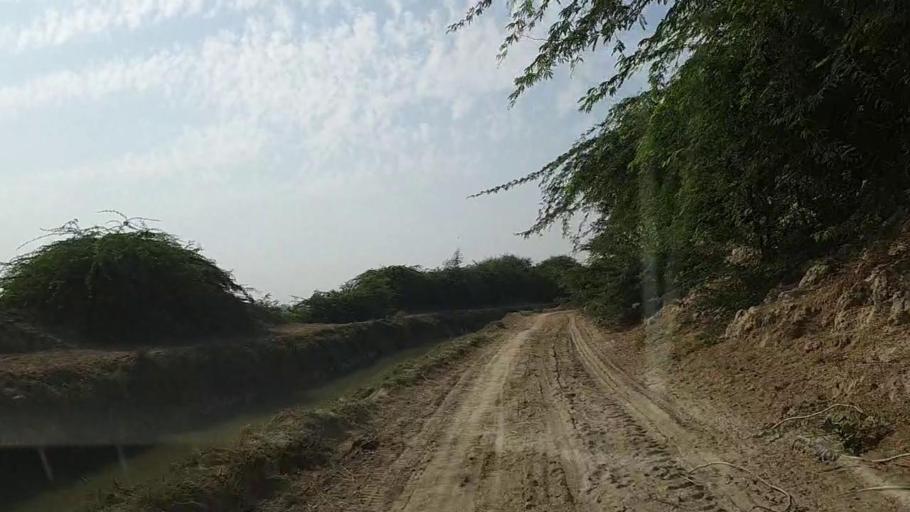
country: PK
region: Sindh
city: Mirpur Batoro
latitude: 24.7058
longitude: 68.3050
